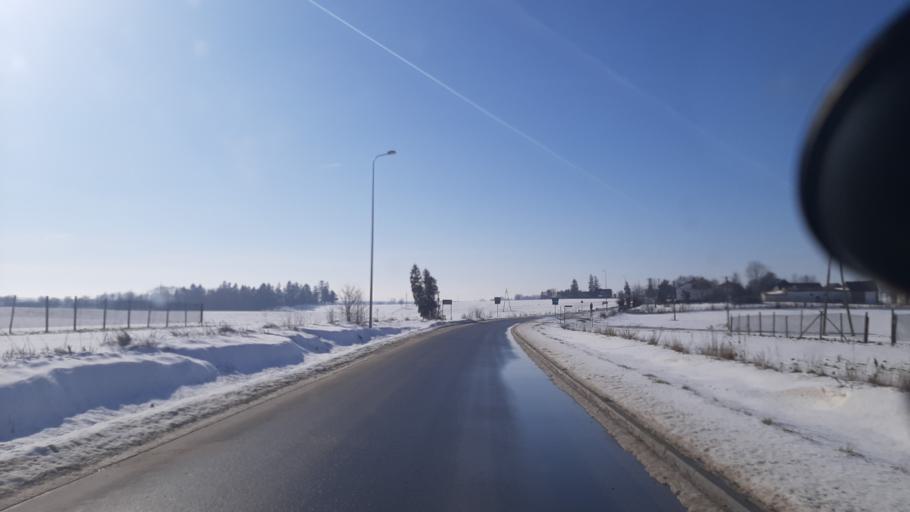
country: PL
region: Lublin Voivodeship
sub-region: Powiat lubelski
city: Garbow
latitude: 51.3321
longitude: 22.3334
